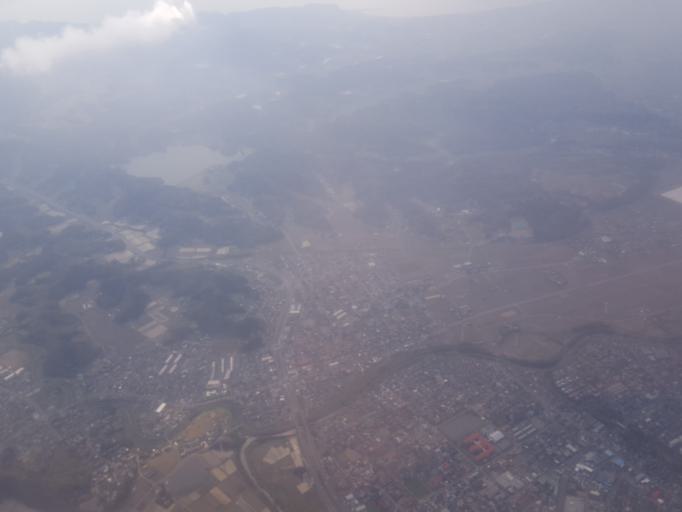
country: JP
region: Chiba
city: Kimitsu
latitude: 35.3194
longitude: 139.9390
